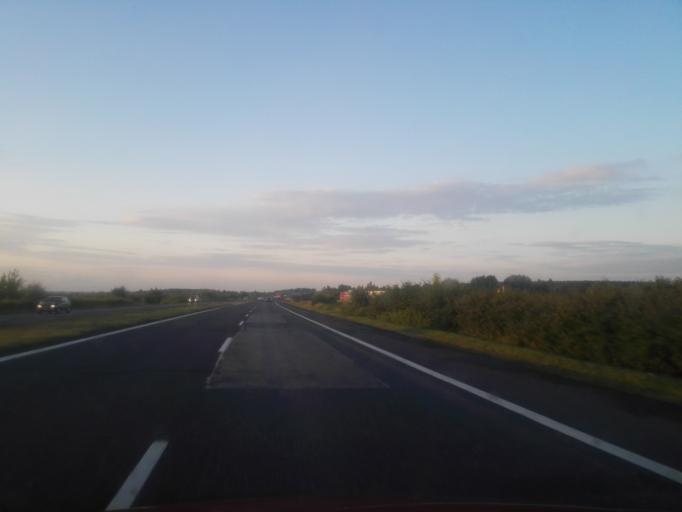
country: PL
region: Silesian Voivodeship
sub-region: Powiat czestochowski
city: Koscielec
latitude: 50.8809
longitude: 19.1658
